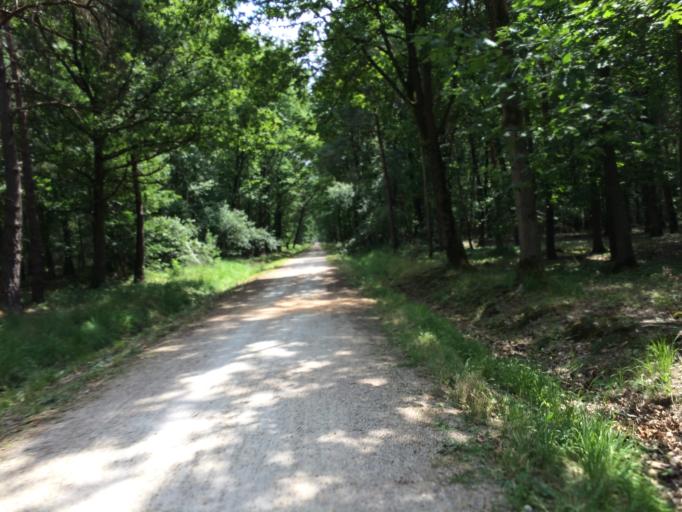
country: FR
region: Ile-de-France
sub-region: Departement de l'Essonne
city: Epinay-sous-Senart
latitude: 48.6702
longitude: 2.4977
